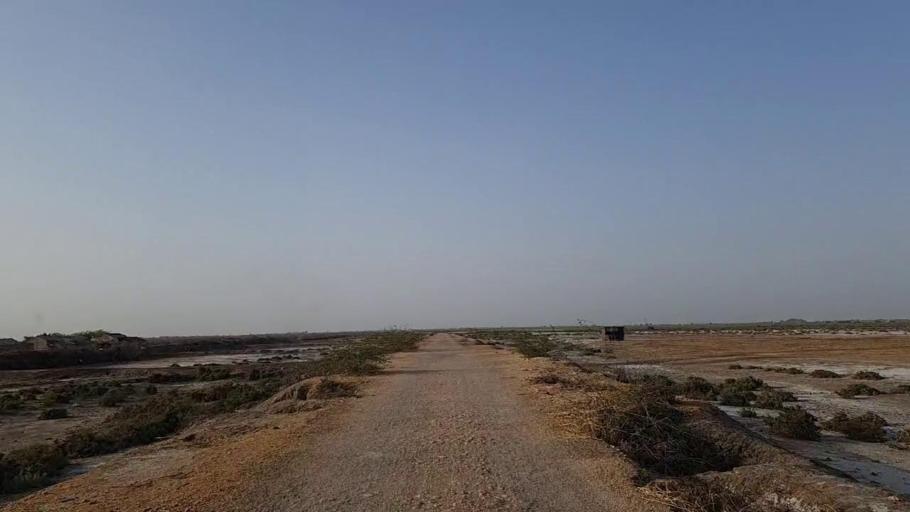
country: PK
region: Sindh
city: Jati
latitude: 24.3477
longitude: 68.1502
